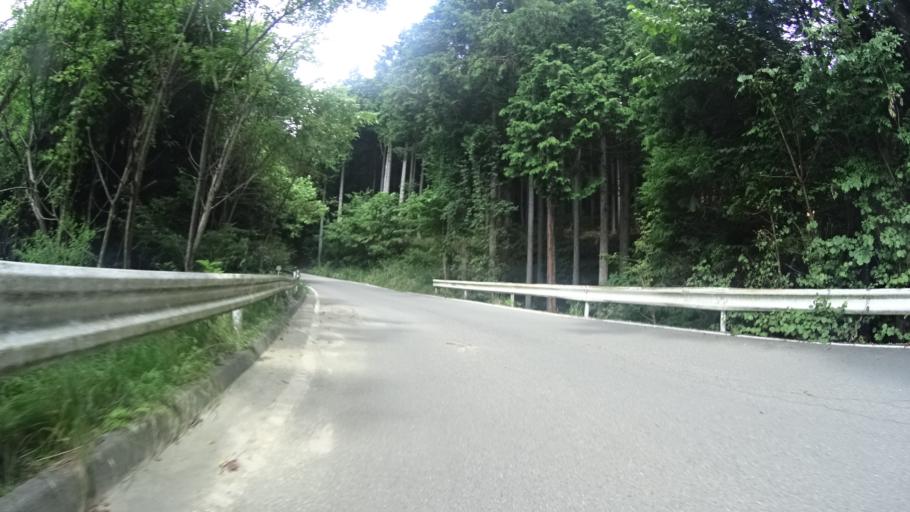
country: JP
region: Yamanashi
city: Enzan
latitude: 35.7861
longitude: 138.6940
